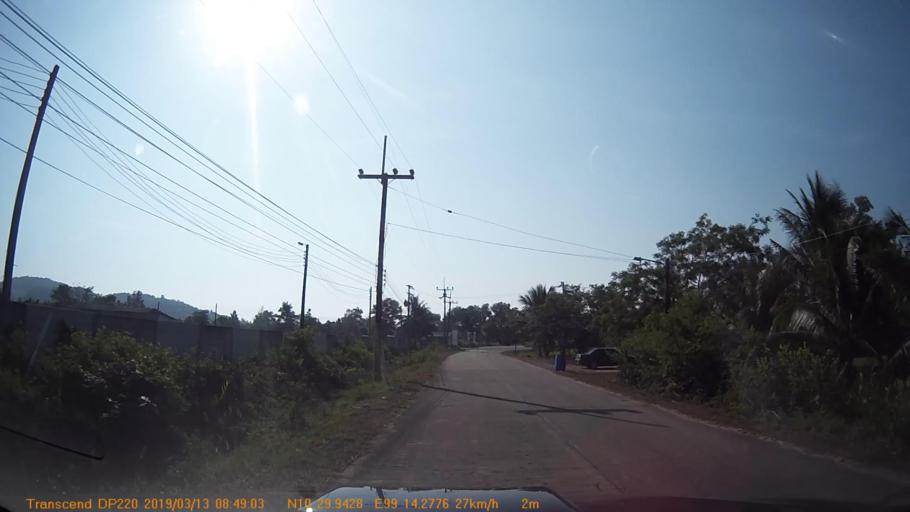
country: TH
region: Chumphon
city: Chumphon
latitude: 10.4989
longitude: 99.2381
